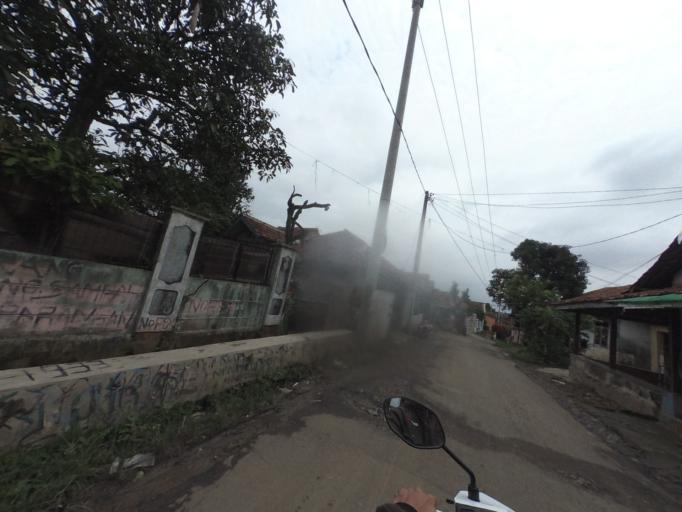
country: ID
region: West Java
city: Bogor
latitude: -6.6122
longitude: 106.7518
